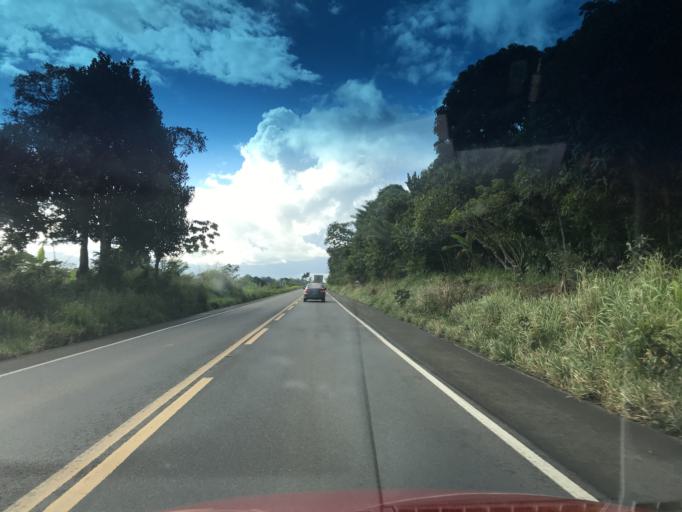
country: BR
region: Bahia
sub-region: Ibirapitanga
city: Ibirapitanga
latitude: -14.1670
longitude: -39.3282
